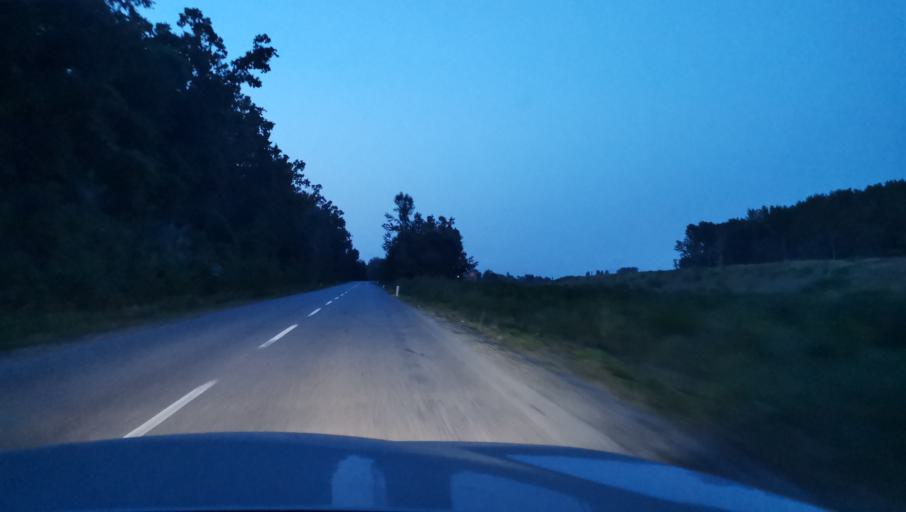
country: RS
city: Boljevci
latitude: 44.7085
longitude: 20.2058
